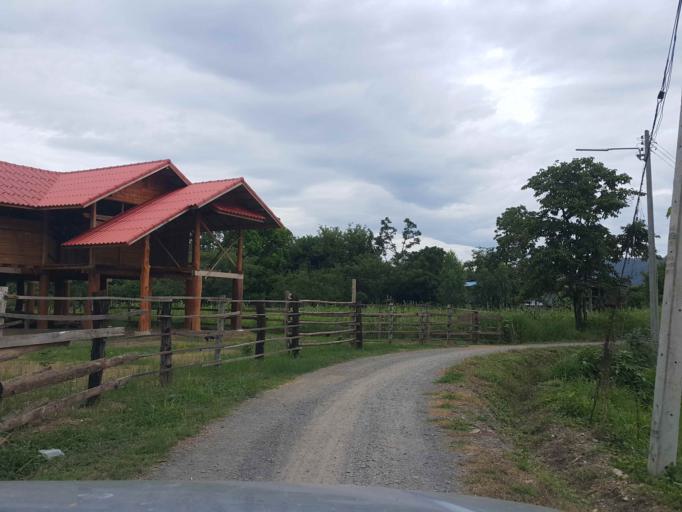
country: TH
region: Sukhothai
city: Thung Saliam
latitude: 17.3252
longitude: 99.4420
